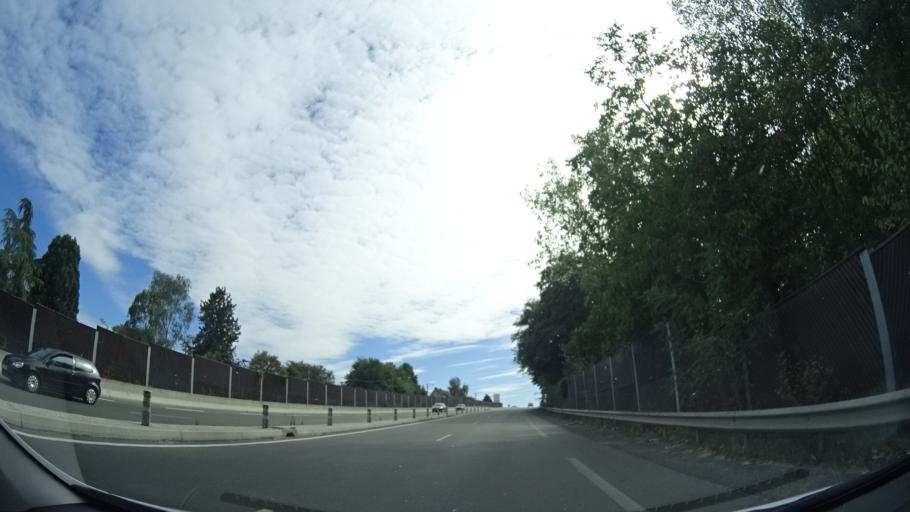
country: FR
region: Centre
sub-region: Departement du Loiret
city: Montargis
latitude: 47.9780
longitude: 2.7416
